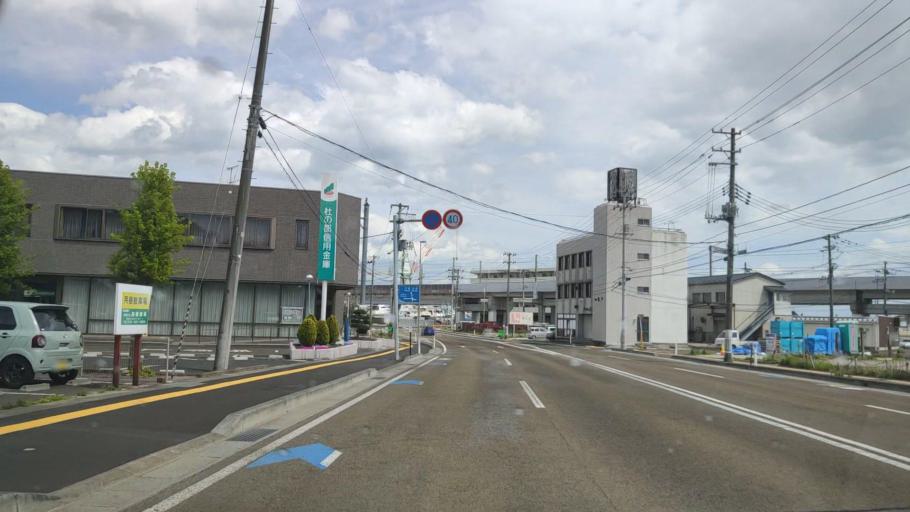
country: JP
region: Miyagi
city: Shiogama
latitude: 38.3241
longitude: 141.0269
